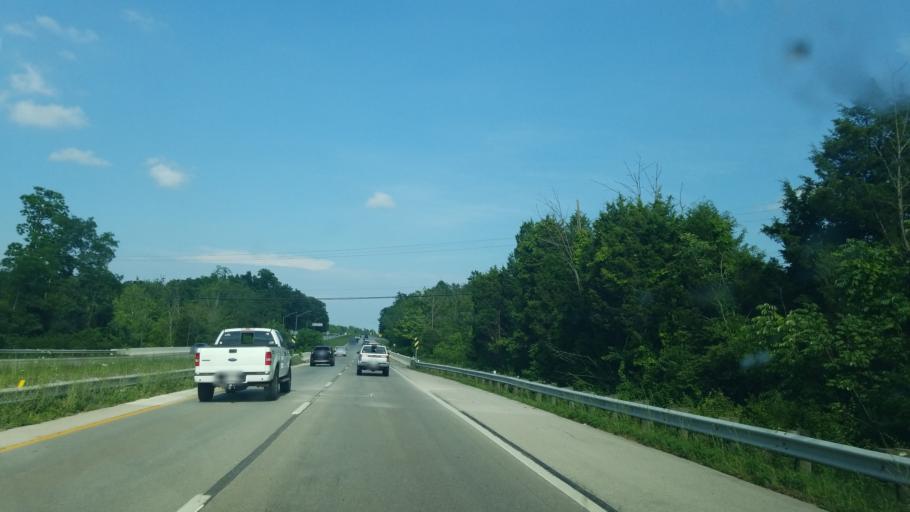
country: US
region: Ohio
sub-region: Clermont County
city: Batavia
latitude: 39.0885
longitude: -84.2230
